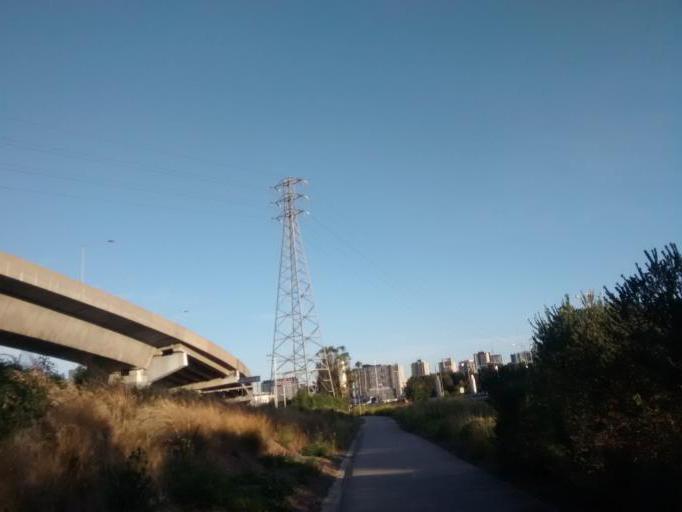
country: AU
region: Victoria
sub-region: Melbourne
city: North Melbourne
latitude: -37.8037
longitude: 144.9359
